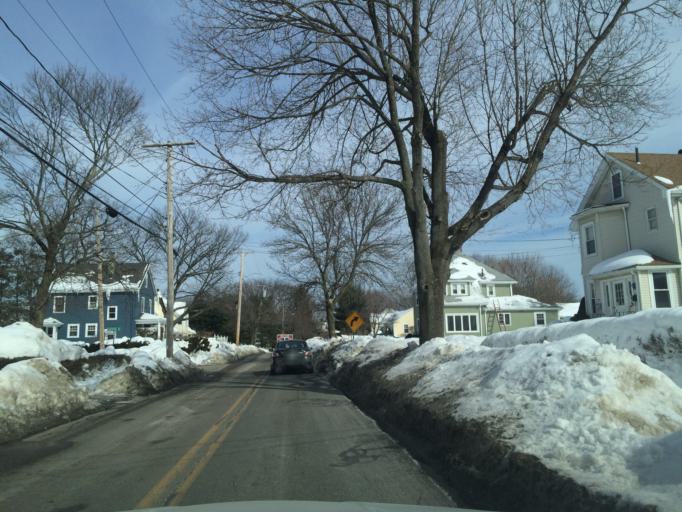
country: US
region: Massachusetts
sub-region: Middlesex County
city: Waltham
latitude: 42.3521
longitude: -71.2375
